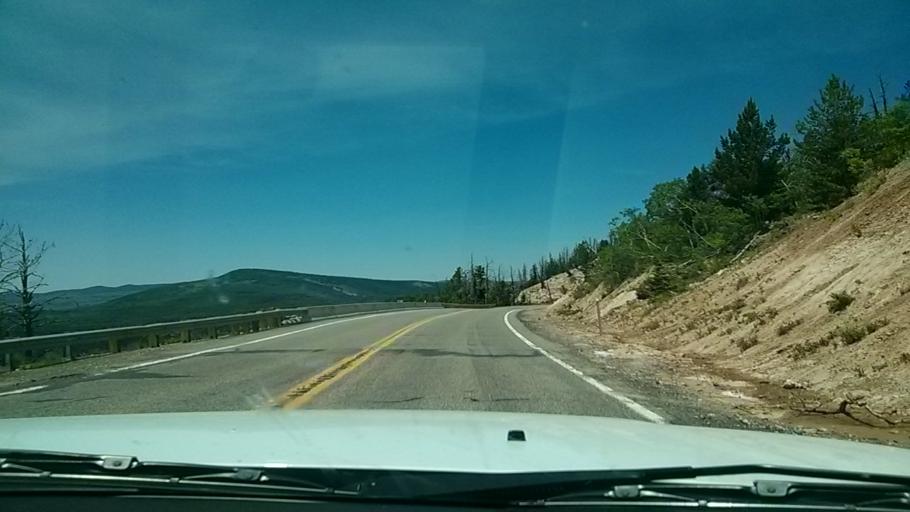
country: US
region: Utah
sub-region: Iron County
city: Cedar City
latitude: 37.5689
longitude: -112.8521
